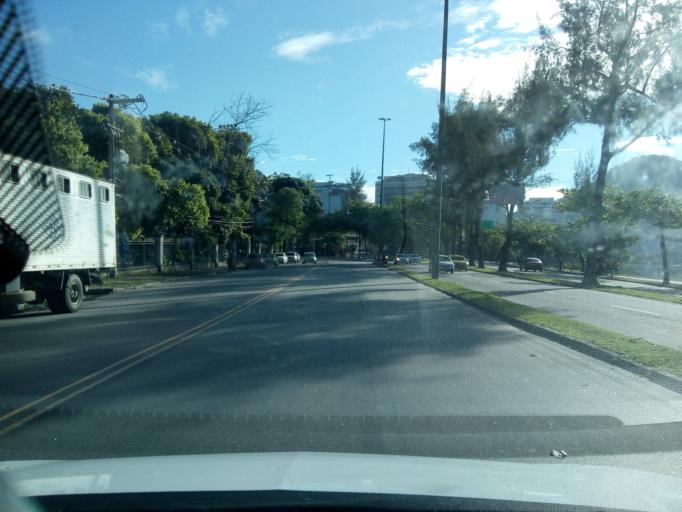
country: BR
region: Rio de Janeiro
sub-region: Rio De Janeiro
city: Rio de Janeiro
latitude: -22.9636
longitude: -43.2137
